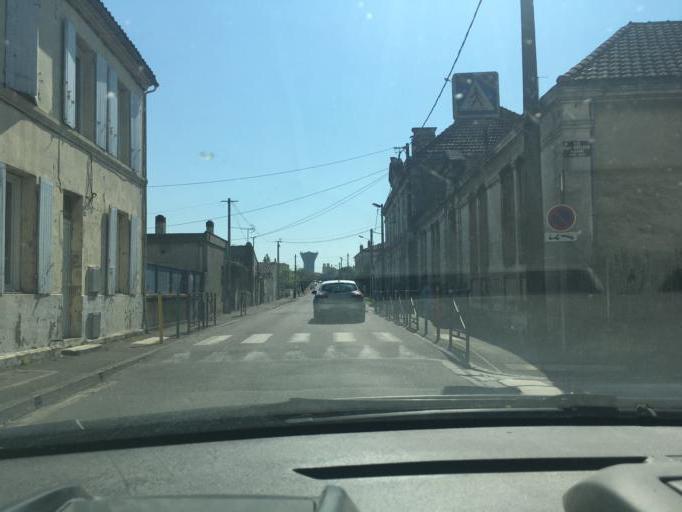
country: FR
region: Poitou-Charentes
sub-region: Departement de la Charente
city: Cognac
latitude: 45.6872
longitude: -0.3331
